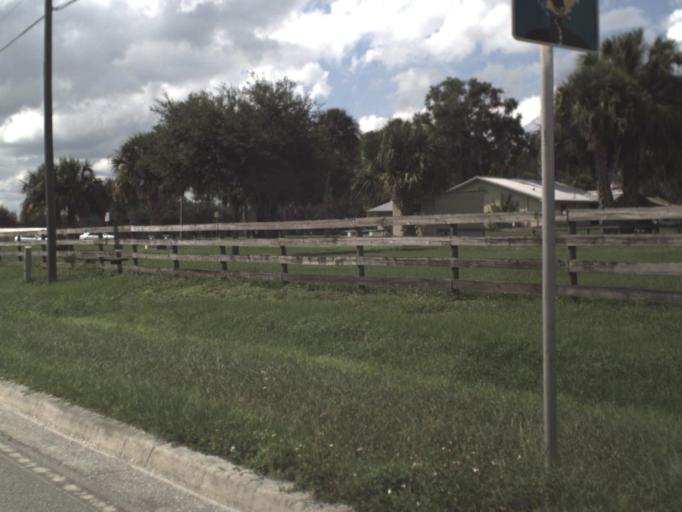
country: US
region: Florida
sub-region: Hardee County
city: Zolfo Springs
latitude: 27.5002
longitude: -81.7992
